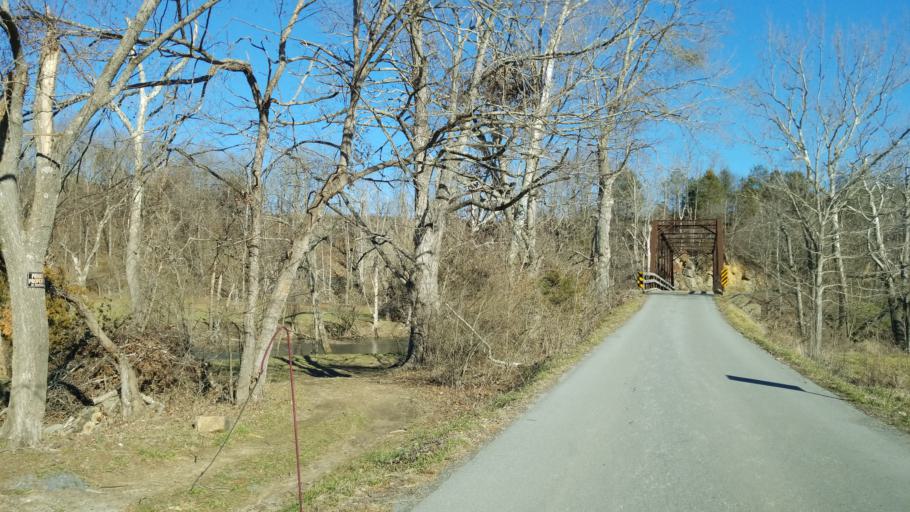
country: US
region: Virginia
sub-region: Pulaski County
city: Pulaski
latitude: 37.1623
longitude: -80.8601
